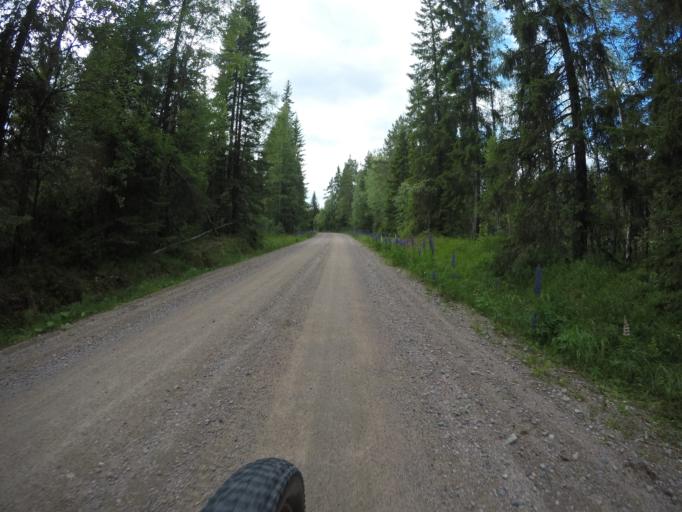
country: SE
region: Vaermland
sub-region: Filipstads Kommun
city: Lesjofors
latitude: 60.1148
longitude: 14.4727
